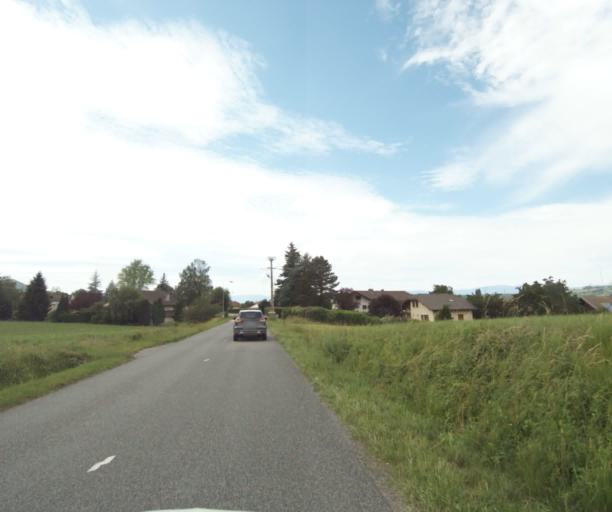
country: FR
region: Rhone-Alpes
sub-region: Departement de la Haute-Savoie
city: Bons-en-Chablais
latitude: 46.2672
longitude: 6.3809
